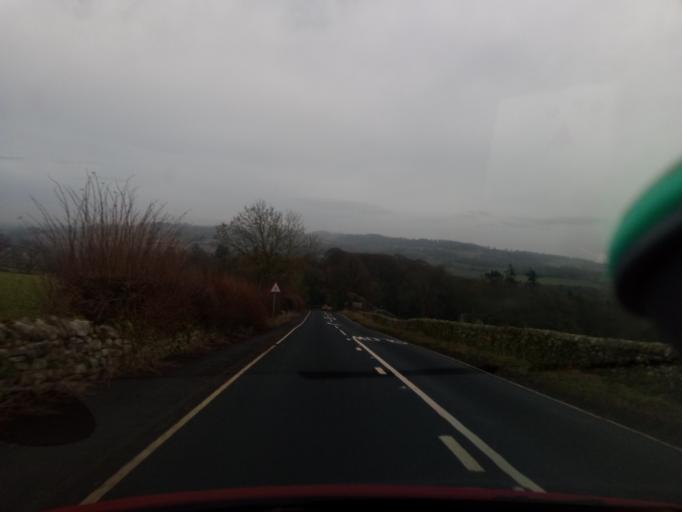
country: GB
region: England
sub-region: Northumberland
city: Wall
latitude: 55.0290
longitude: -2.1510
